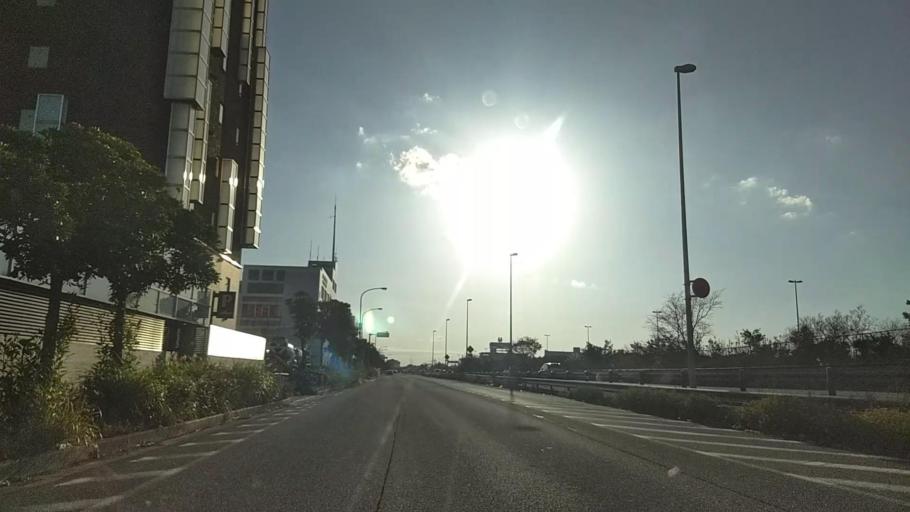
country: JP
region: Tokyo
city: Urayasu
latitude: 35.6689
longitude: 139.9240
